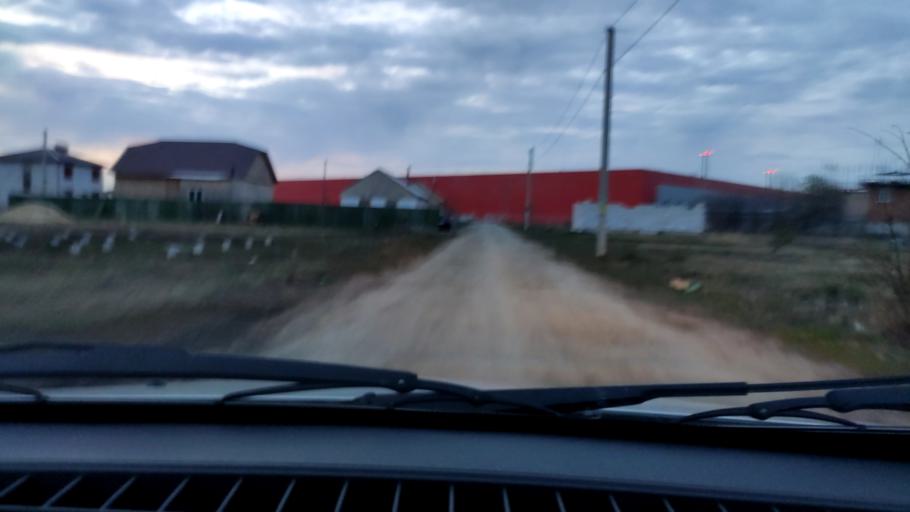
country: RU
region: Voronezj
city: Podgornoye
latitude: 51.7984
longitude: 39.2150
